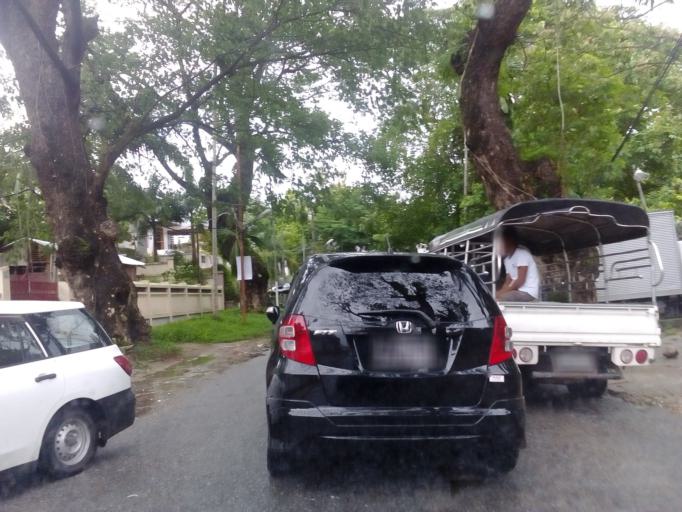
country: MM
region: Yangon
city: Yangon
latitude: 16.8143
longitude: 96.1486
